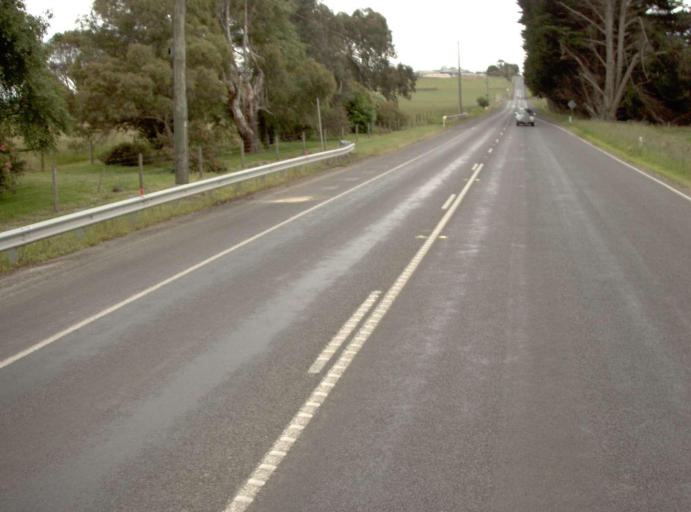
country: AU
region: Victoria
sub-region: Baw Baw
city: Warragul
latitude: -38.4962
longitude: 145.9520
